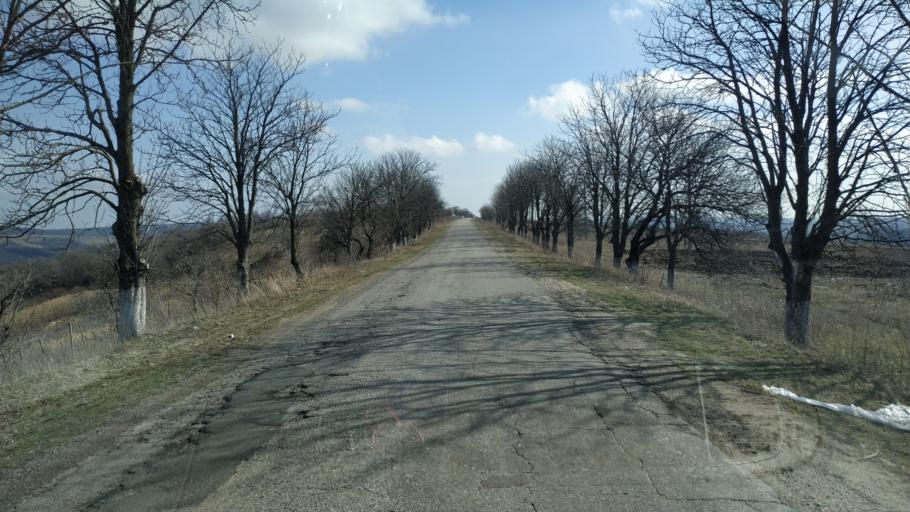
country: MD
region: Hincesti
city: Hincesti
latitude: 46.8531
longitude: 28.6440
